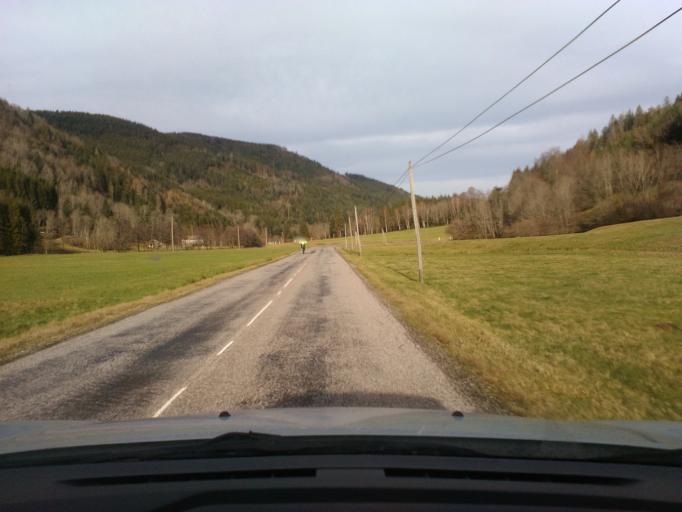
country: FR
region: Lorraine
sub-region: Departement des Vosges
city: Xonrupt-Longemer
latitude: 48.1278
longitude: 6.9554
